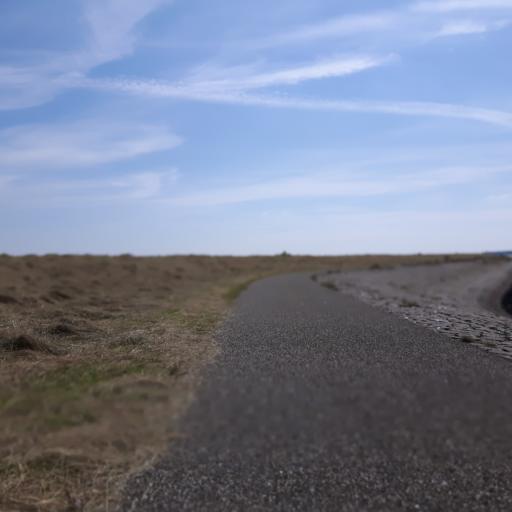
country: NL
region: Zeeland
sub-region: Schouwen-Duiveland
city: Bruinisse
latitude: 51.6377
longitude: 4.0993
